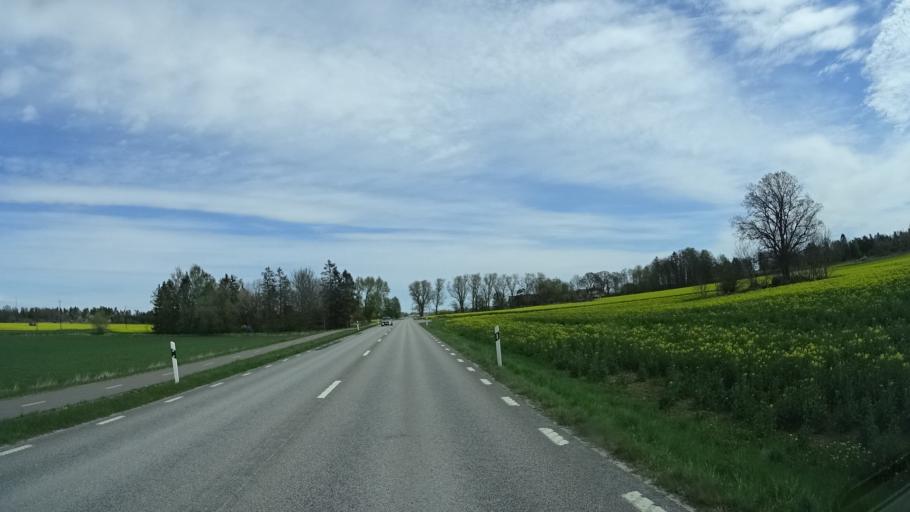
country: SE
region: OEstergoetland
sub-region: Linkopings Kommun
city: Vikingstad
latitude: 58.3721
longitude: 15.3962
